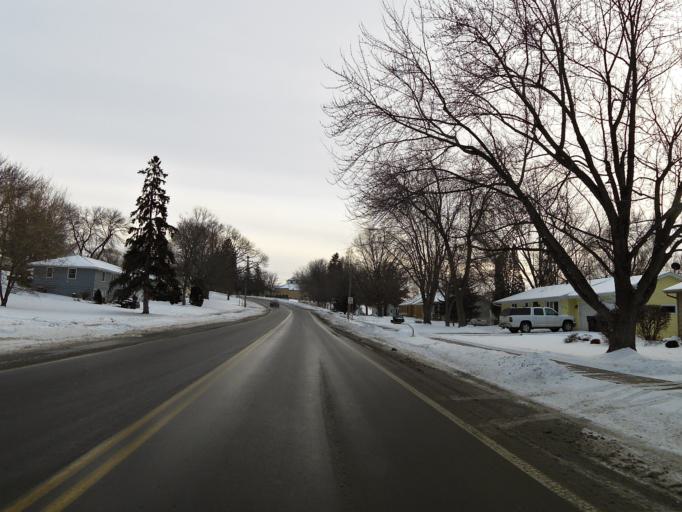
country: US
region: Minnesota
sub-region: Carver County
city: Victoria
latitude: 44.8577
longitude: -93.6620
